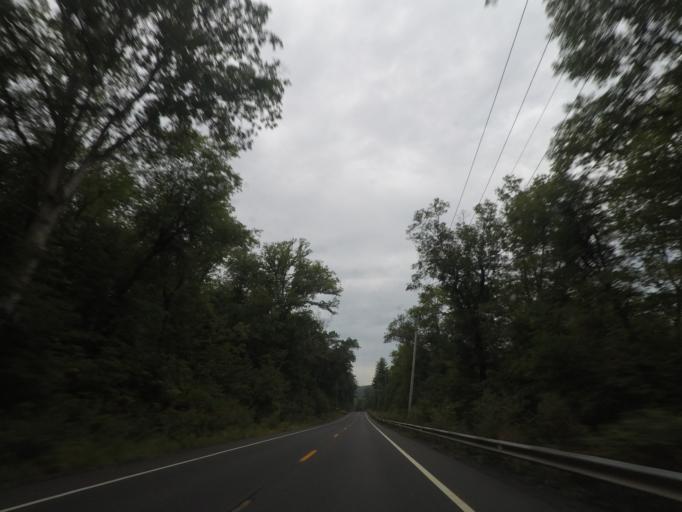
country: US
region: Massachusetts
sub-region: Hampden County
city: Palmer
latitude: 42.1885
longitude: -72.2645
